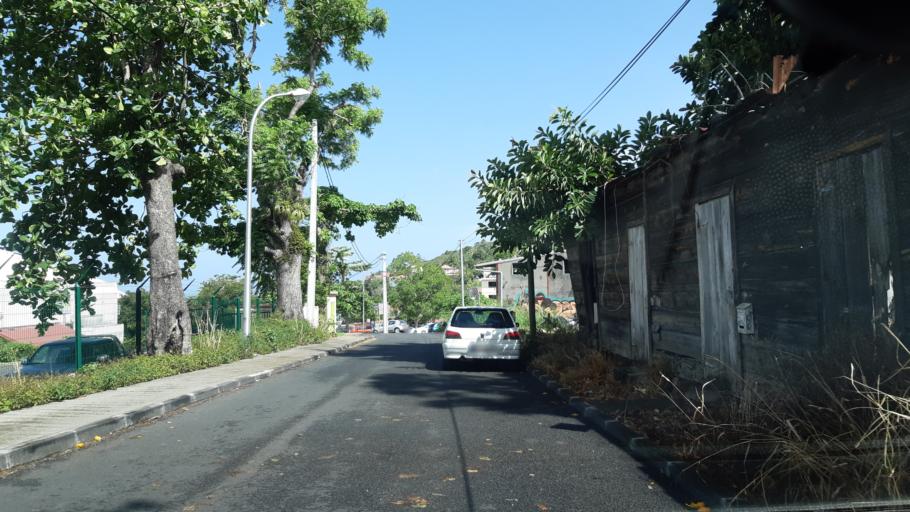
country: GP
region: Guadeloupe
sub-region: Guadeloupe
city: Basse-Terre
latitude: 16.0014
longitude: -61.7164
